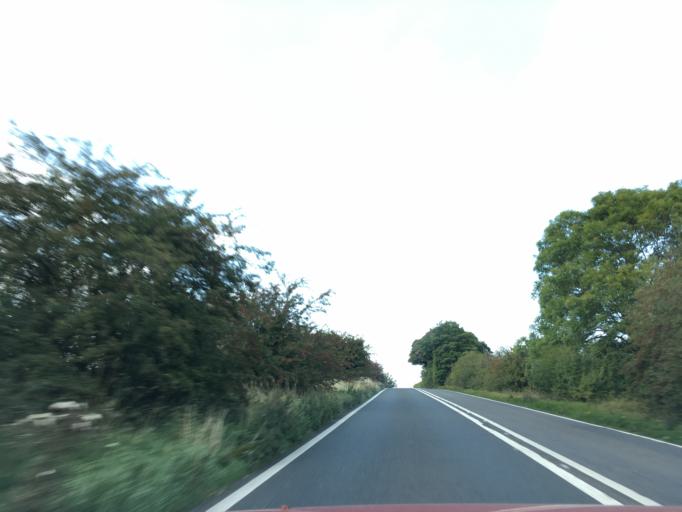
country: GB
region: England
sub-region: Gloucestershire
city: Northleach
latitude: 51.8577
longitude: -1.8018
